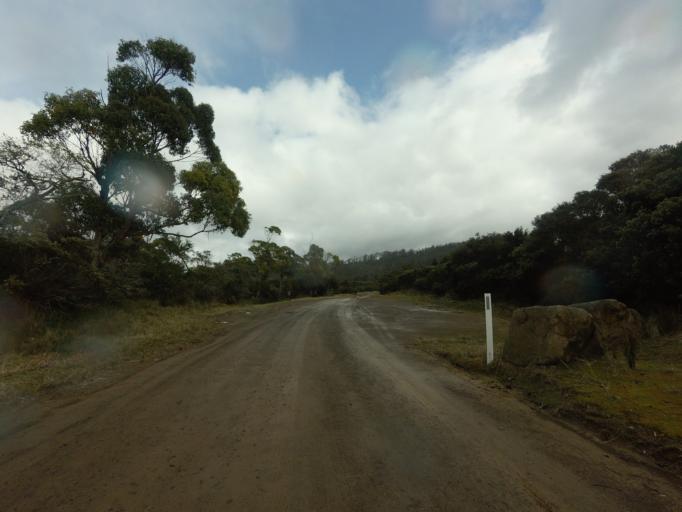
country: AU
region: Tasmania
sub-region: Huon Valley
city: Geeveston
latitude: -43.5824
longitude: 146.8916
